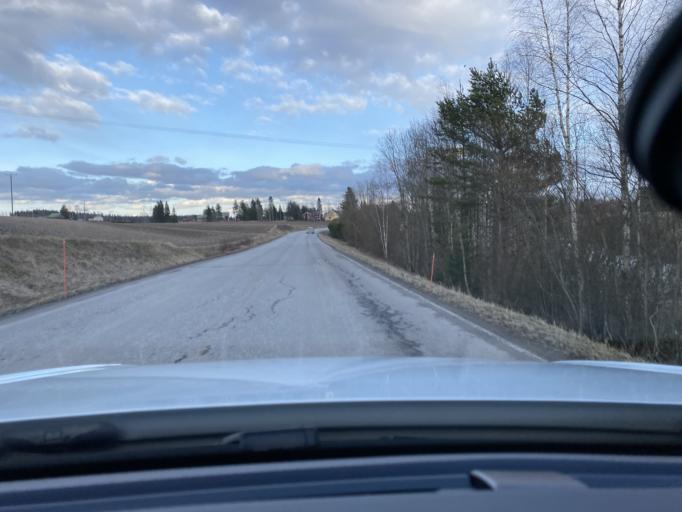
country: FI
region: Pirkanmaa
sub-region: Lounais-Pirkanmaa
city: Punkalaidun
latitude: 61.1224
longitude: 23.0380
